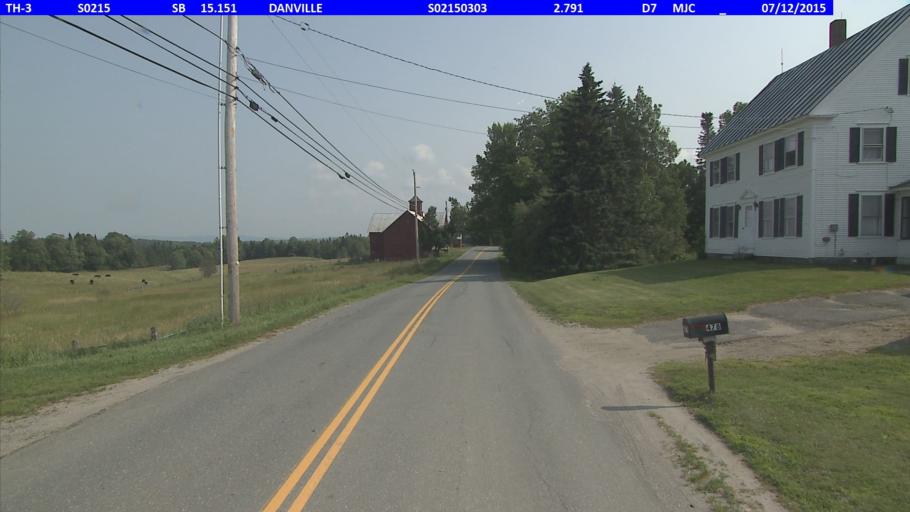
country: US
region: Vermont
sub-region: Caledonia County
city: Saint Johnsbury
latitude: 44.4051
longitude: -72.1415
